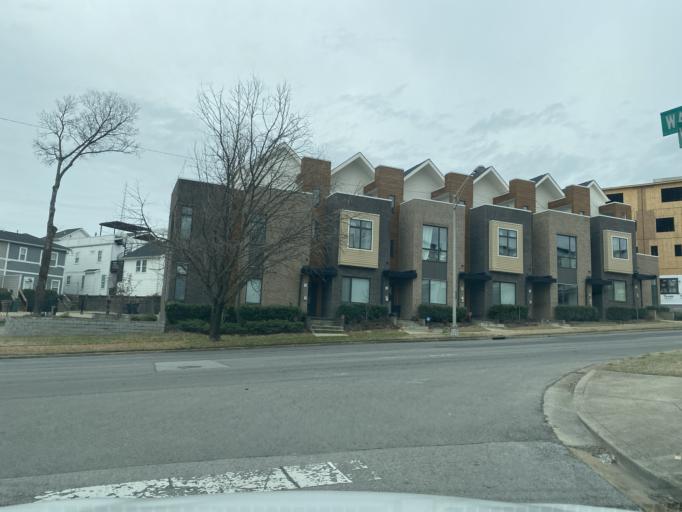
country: US
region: Tennessee
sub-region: Davidson County
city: Nashville
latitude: 36.1355
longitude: -86.7857
